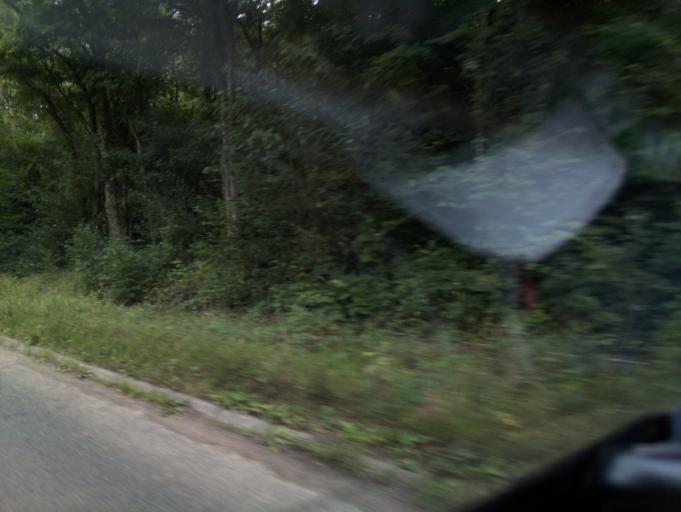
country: GB
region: England
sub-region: Devon
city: Bradninch
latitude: 50.8075
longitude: -3.4259
